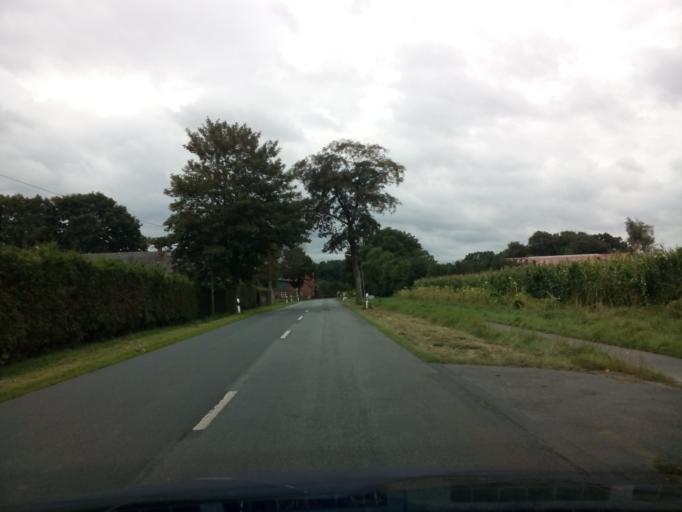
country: DE
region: Lower Saxony
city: Beverstedt
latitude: 53.4477
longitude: 8.8320
